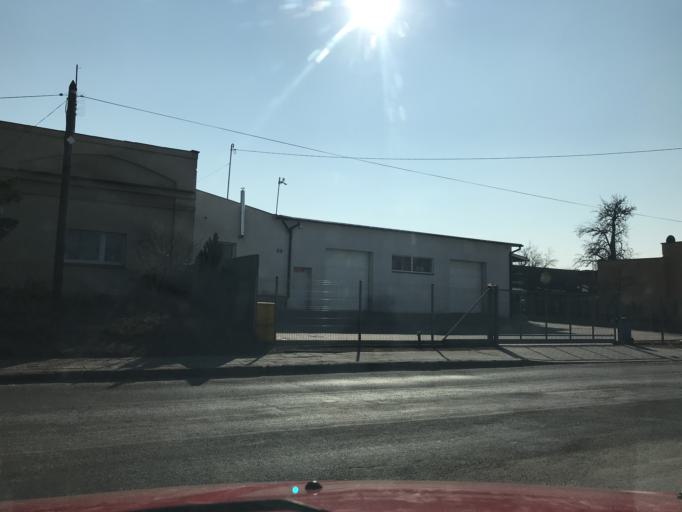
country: PL
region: Greater Poland Voivodeship
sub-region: Kalisz
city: Kalisz
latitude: 51.7572
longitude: 18.0627
